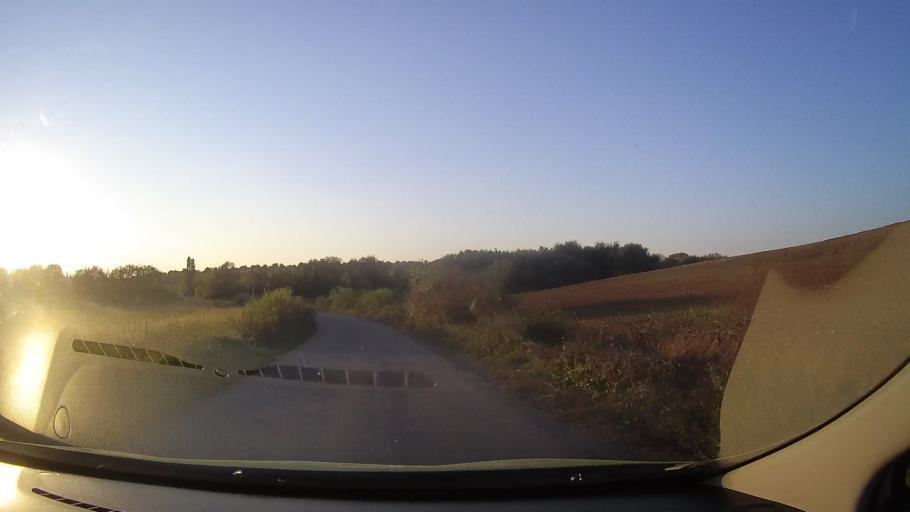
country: RO
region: Bihor
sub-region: Comuna Salard
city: Salard
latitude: 47.2497
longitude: 22.0145
